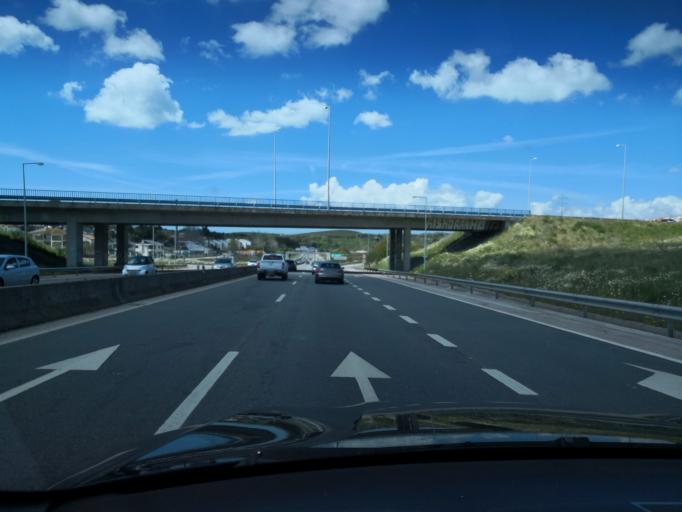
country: PT
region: Setubal
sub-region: Almada
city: Caparica
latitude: 38.6541
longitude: -9.2144
